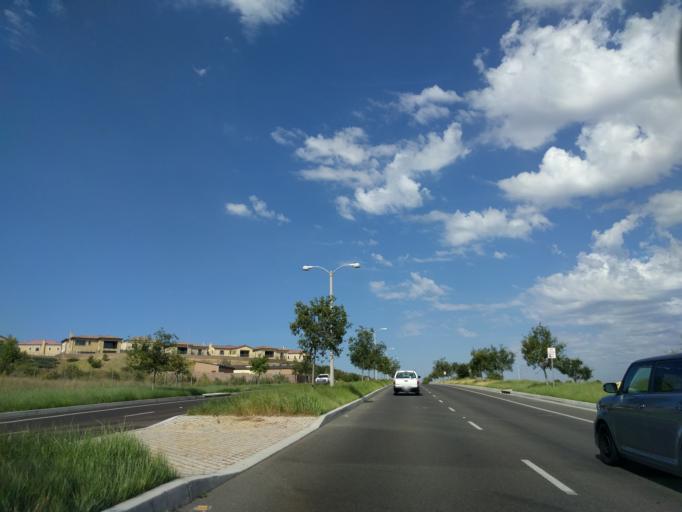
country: US
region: California
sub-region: Orange County
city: Laguna Woods
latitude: 33.6353
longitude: -117.7509
